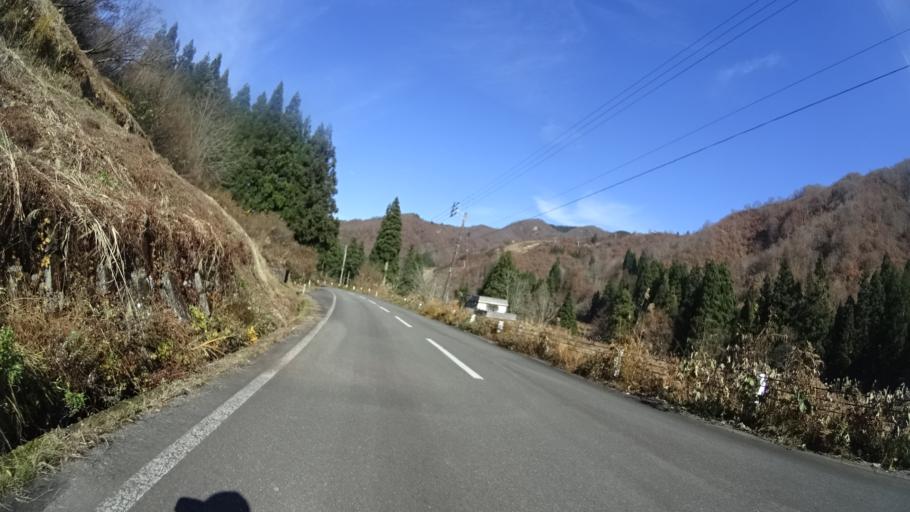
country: JP
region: Niigata
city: Muikamachi
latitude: 37.1882
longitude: 139.0818
